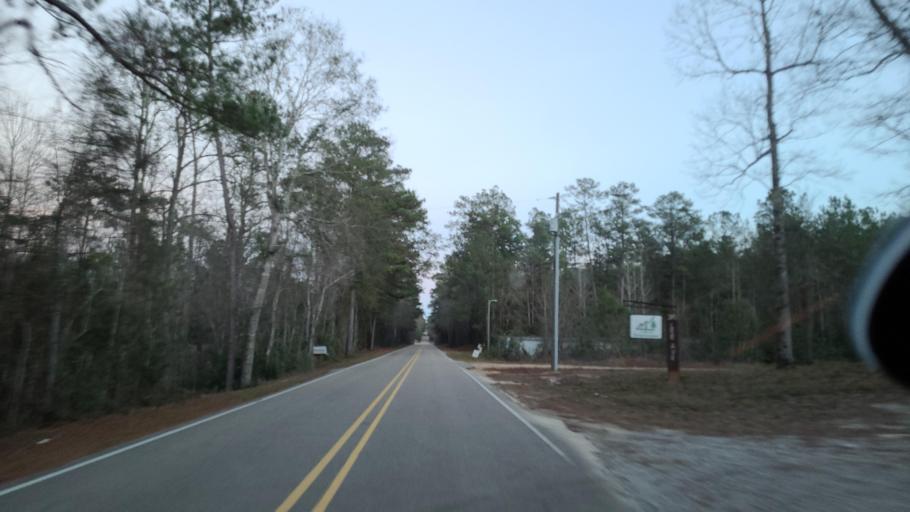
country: US
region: Mississippi
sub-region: Forrest County
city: Hattiesburg
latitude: 31.2122
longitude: -89.2594
